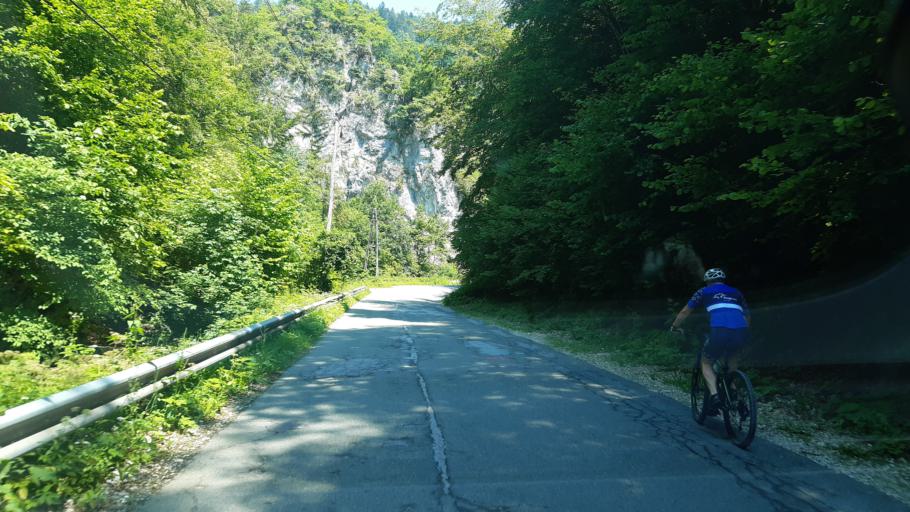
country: SI
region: Cerklje na Gorenjskem
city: Cerklje na Gorenjskem
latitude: 46.2824
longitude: 14.4948
